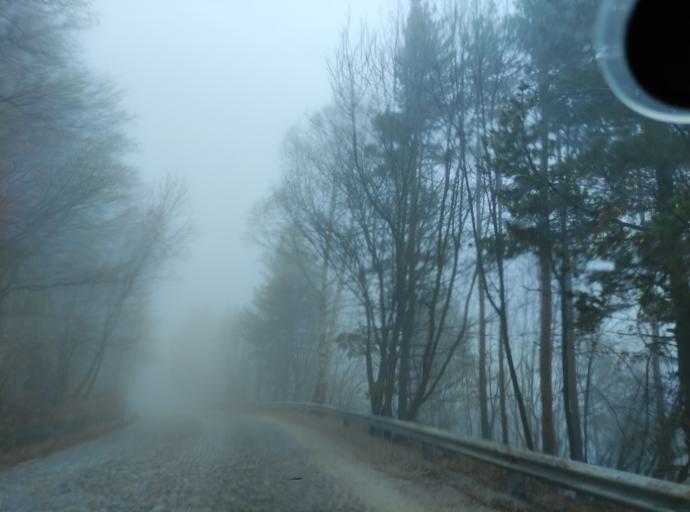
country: BG
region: Sofia-Capital
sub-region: Stolichna Obshtina
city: Sofia
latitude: 42.6239
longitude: 23.2933
